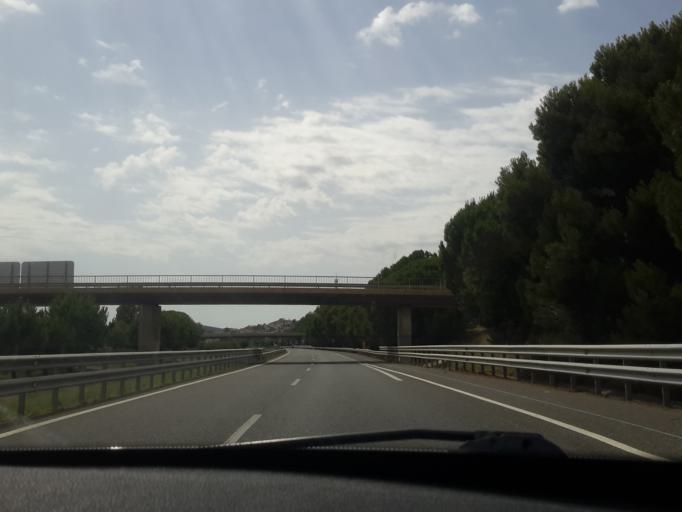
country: ES
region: Catalonia
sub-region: Provincia de Tarragona
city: la Bisbal del Penedes
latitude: 41.2847
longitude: 1.4922
